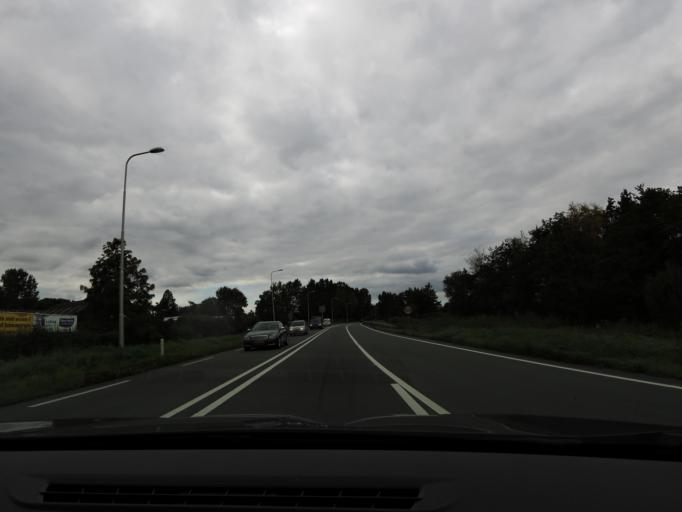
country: NL
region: South Holland
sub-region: Gemeente Krimpen aan den IJssel
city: Krimpen aan den IJssel
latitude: 51.9074
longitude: 4.5979
